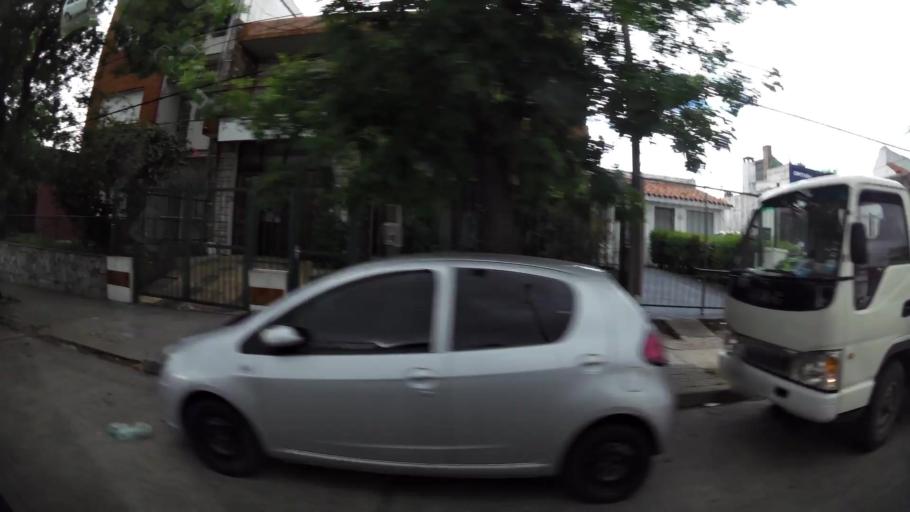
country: UY
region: Montevideo
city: Montevideo
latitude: -34.8710
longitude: -56.1587
